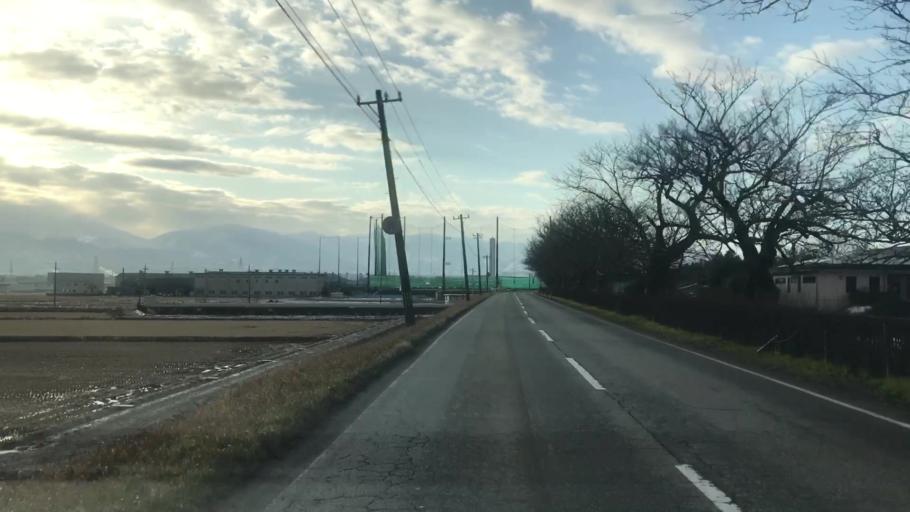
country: JP
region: Toyama
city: Toyama-shi
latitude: 36.6993
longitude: 137.2818
